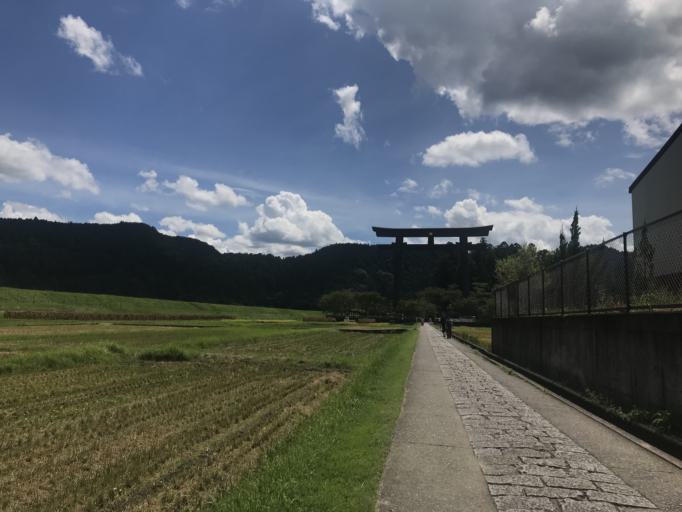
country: JP
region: Wakayama
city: Shingu
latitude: 33.8376
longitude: 135.7756
